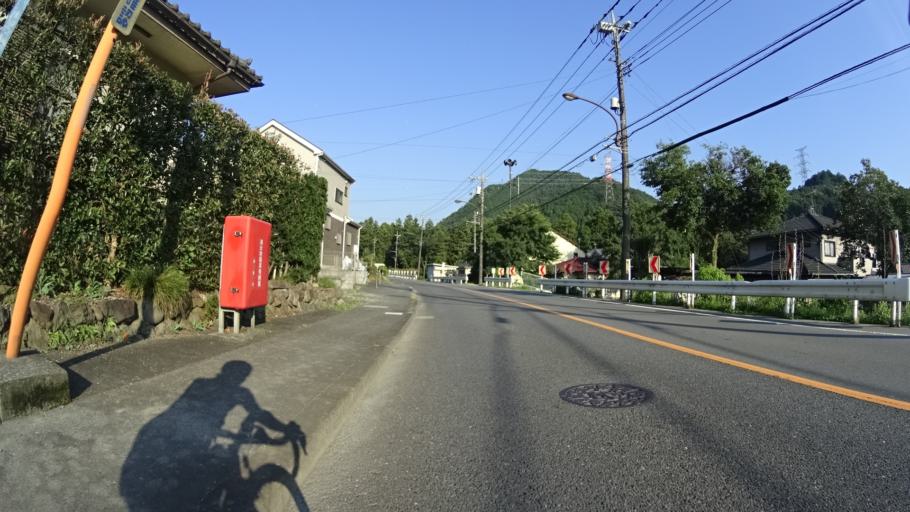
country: JP
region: Tokyo
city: Ome
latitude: 35.8036
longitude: 139.2068
